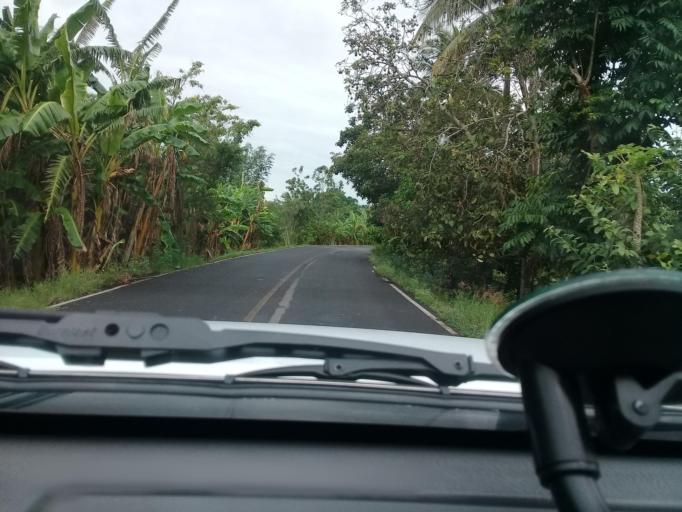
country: MX
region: Veracruz
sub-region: Paso de Ovejas
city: El Hatito
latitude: 19.3204
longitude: -96.3892
